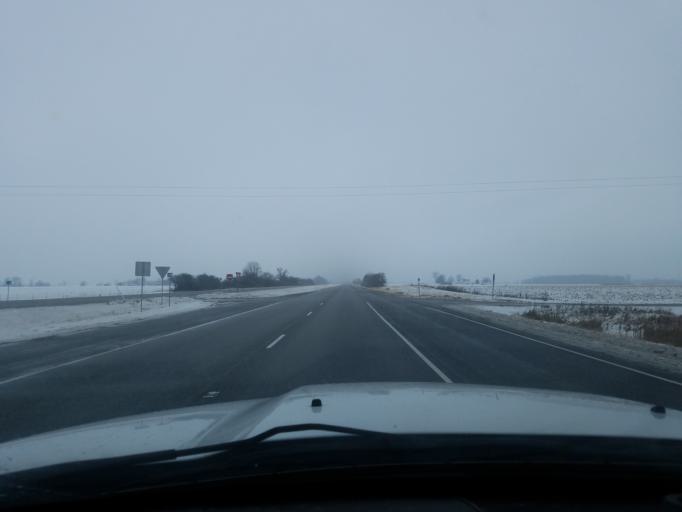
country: US
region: Indiana
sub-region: Fulton County
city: Rochester
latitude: 40.9818
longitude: -86.1679
